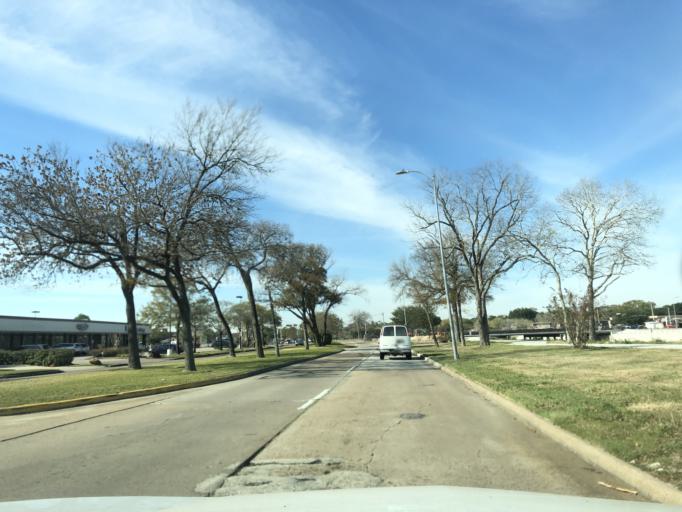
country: US
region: Texas
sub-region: Harris County
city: Bellaire
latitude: 29.6769
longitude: -95.4916
